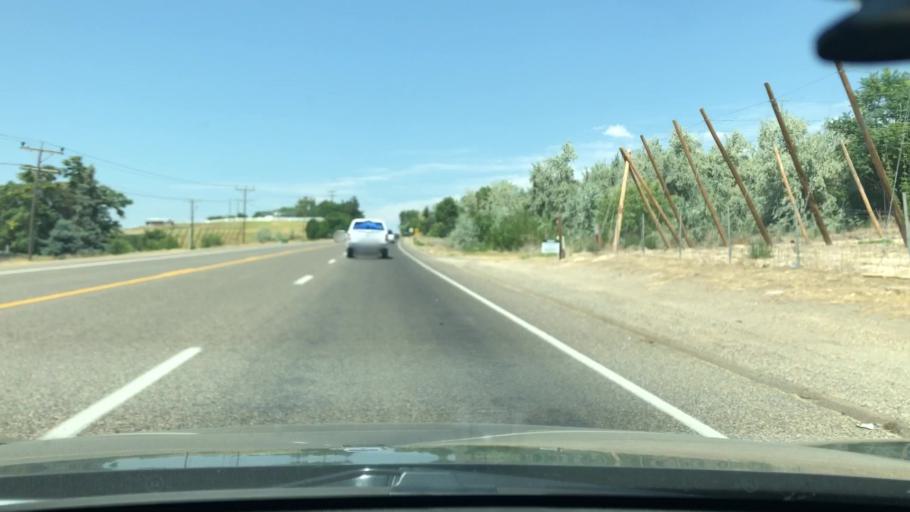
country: US
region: Idaho
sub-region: Canyon County
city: Wilder
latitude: 43.6567
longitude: -116.9118
